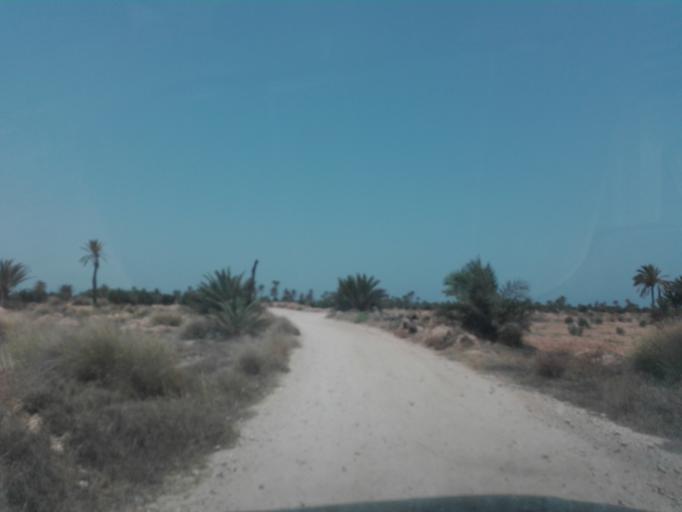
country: TN
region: Safaqis
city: Al Qarmadah
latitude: 34.6633
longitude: 11.0980
